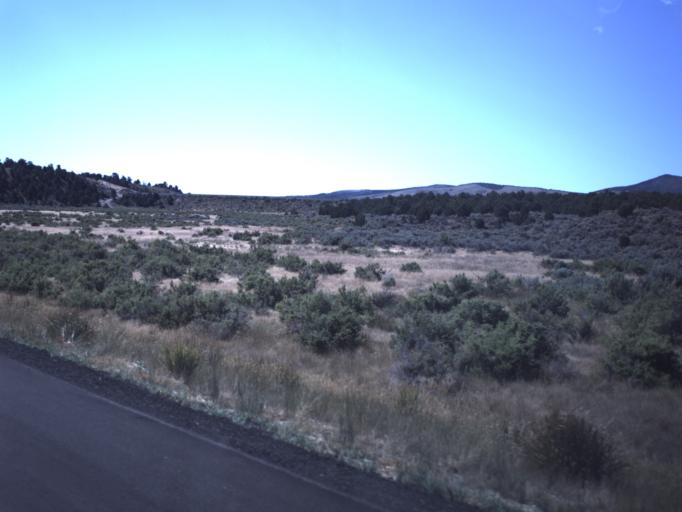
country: US
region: Utah
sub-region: Utah County
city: Eagle Mountain
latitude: 40.0012
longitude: -112.2748
